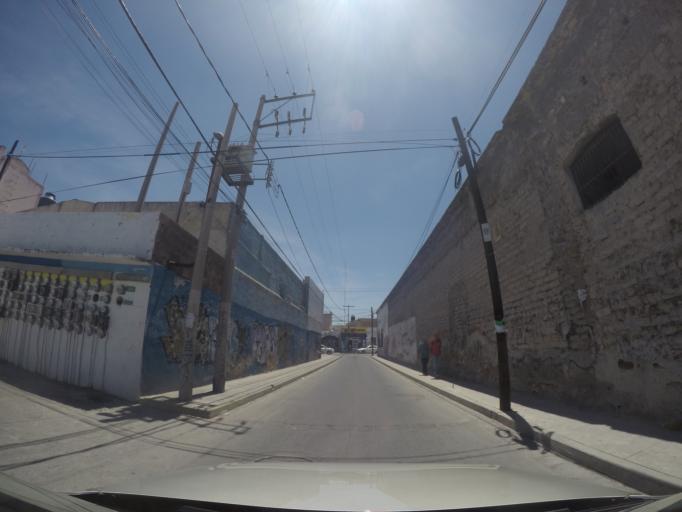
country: MX
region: San Luis Potosi
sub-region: San Luis Potosi
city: San Luis Potosi
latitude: 22.1565
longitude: -100.9831
